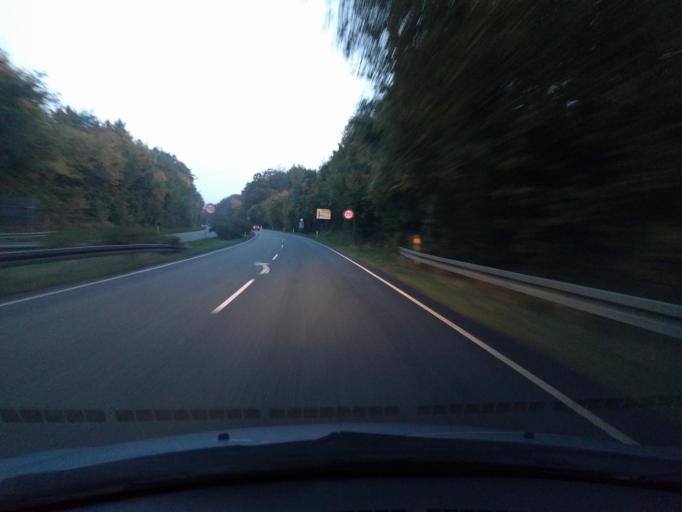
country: DK
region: South Denmark
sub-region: Svendborg Kommune
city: Svendborg
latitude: 55.0566
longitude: 10.5905
